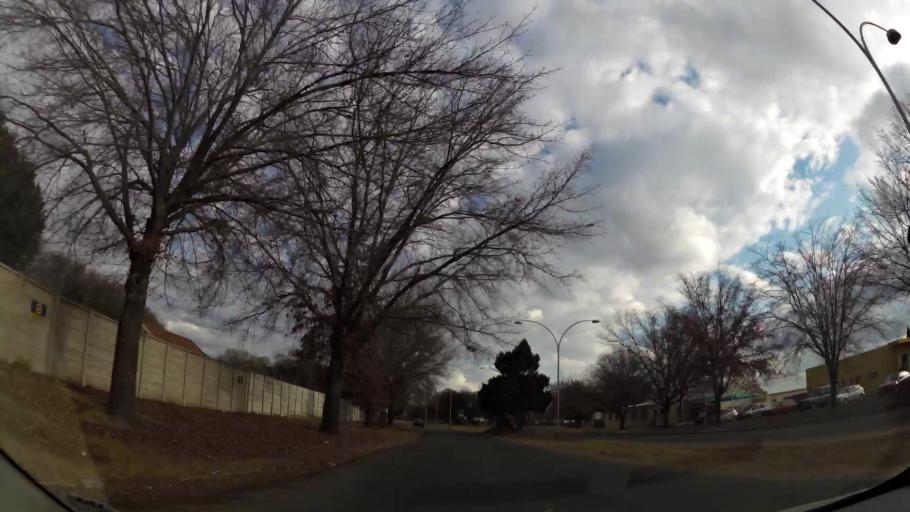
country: ZA
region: Orange Free State
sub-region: Fezile Dabi District Municipality
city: Sasolburg
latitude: -26.8031
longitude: 27.8173
